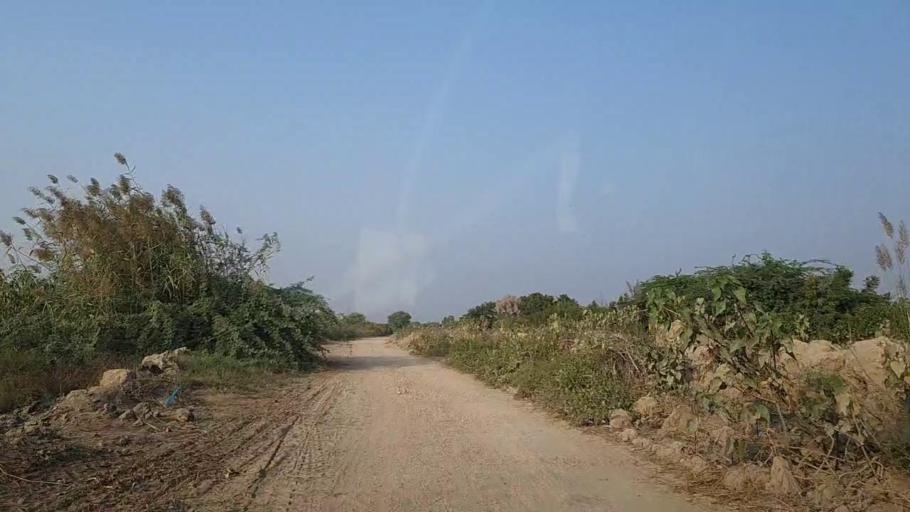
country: PK
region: Sindh
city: Thatta
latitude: 24.6864
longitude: 67.7902
